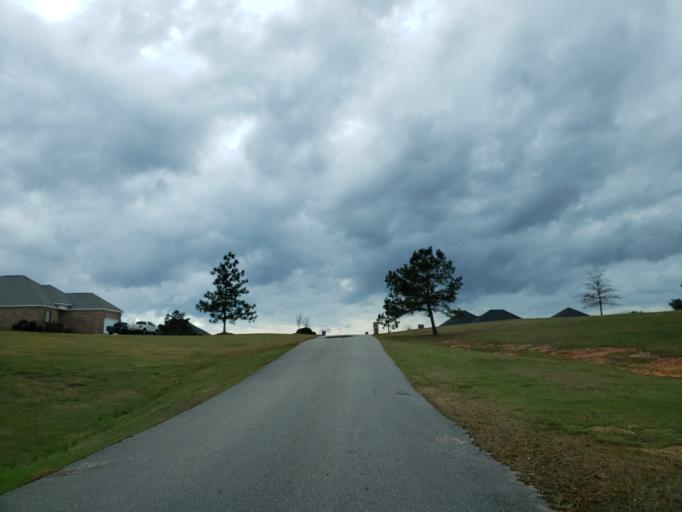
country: US
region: Mississippi
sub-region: Jones County
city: Ellisville
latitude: 31.5513
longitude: -89.2534
